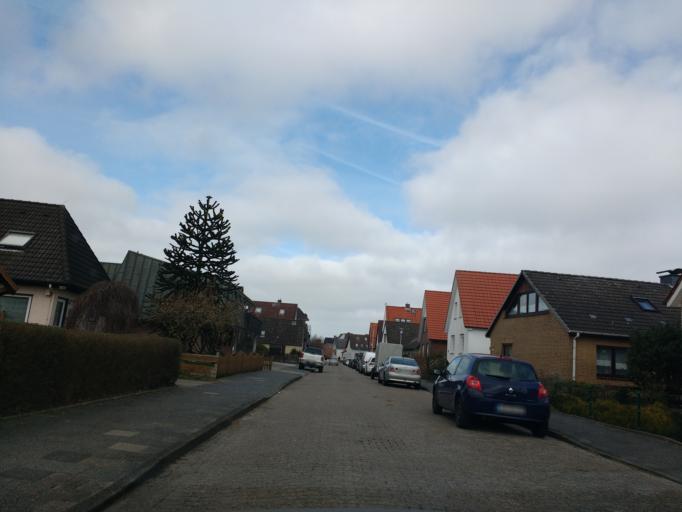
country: DE
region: Lower Saxony
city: Cuxhaven
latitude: 53.8825
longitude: 8.6436
